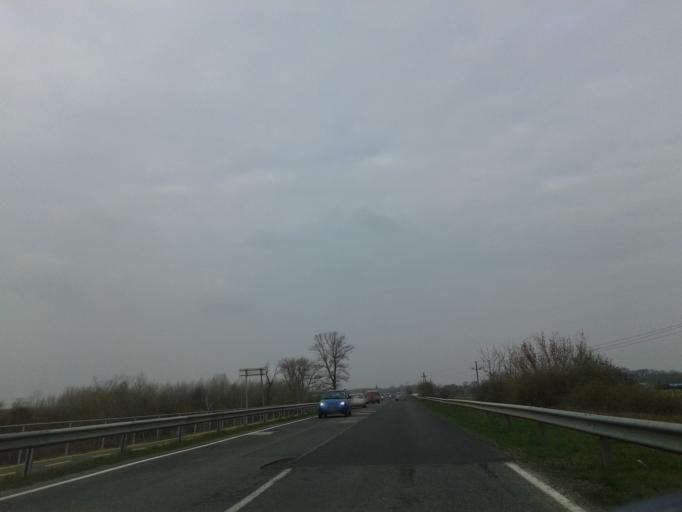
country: HU
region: Gyor-Moson-Sopron
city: Bony
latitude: 47.7326
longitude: 17.8015
